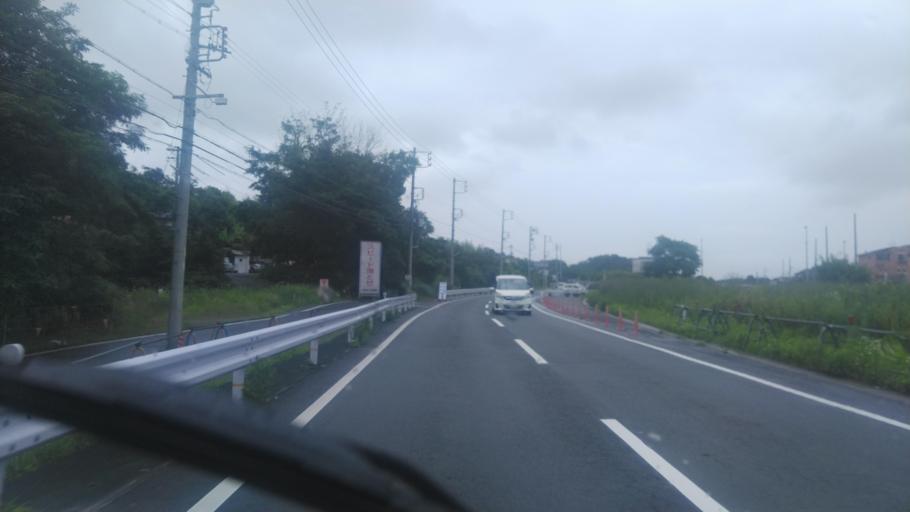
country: JP
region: Aichi
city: Kasugai
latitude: 35.2408
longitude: 137.0256
